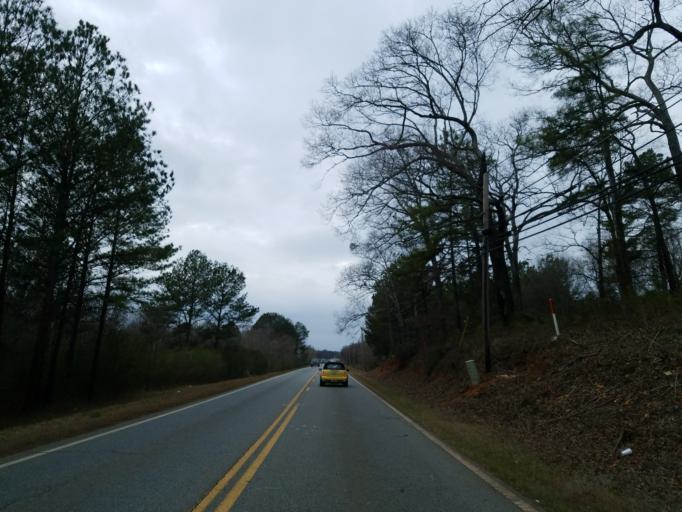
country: US
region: Georgia
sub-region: Bartow County
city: Emerson
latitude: 34.1504
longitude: -84.7752
